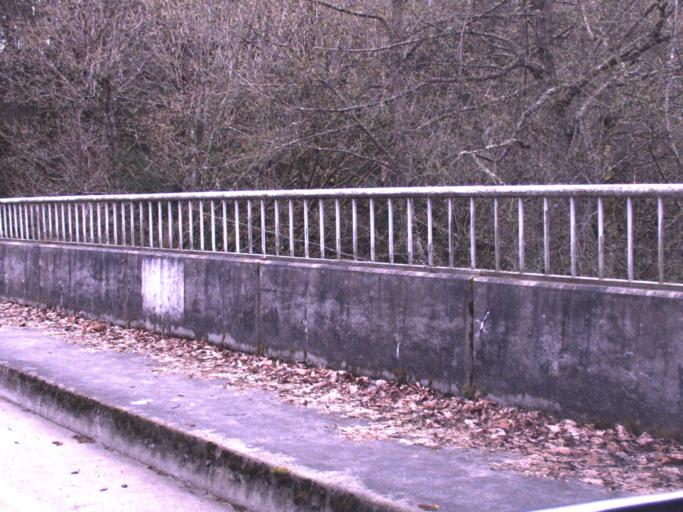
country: US
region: Washington
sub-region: King County
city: Federal Way
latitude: 47.3268
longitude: -122.3768
